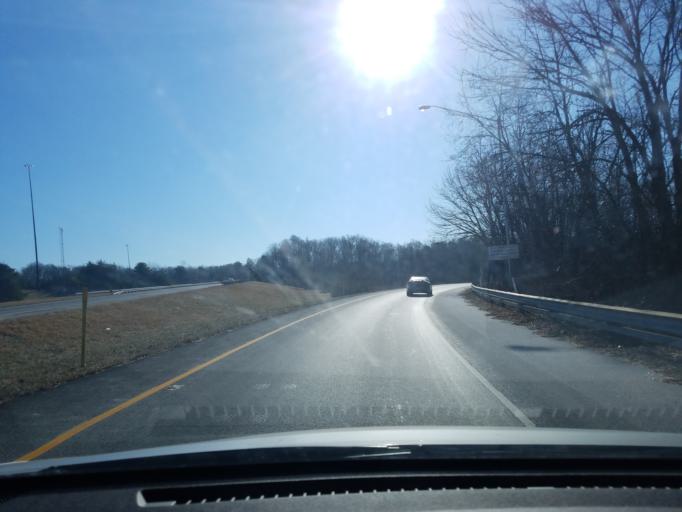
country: US
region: Indiana
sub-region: Floyd County
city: Galena
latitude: 38.3041
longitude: -85.8918
